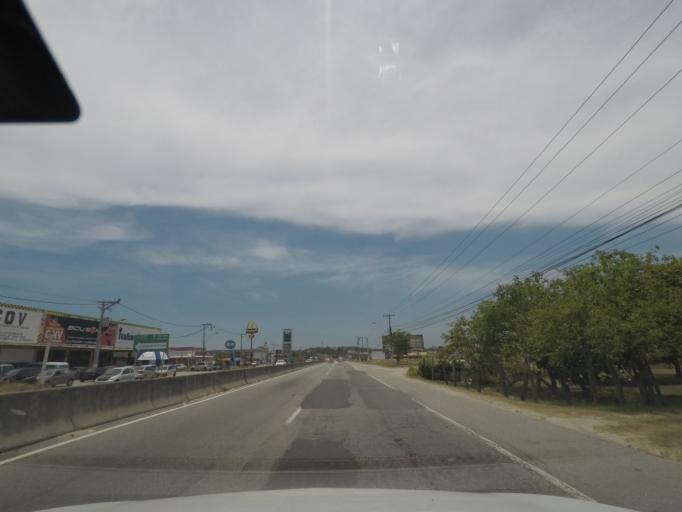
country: BR
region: Rio de Janeiro
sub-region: Marica
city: Marica
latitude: -22.9276
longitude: -42.8683
